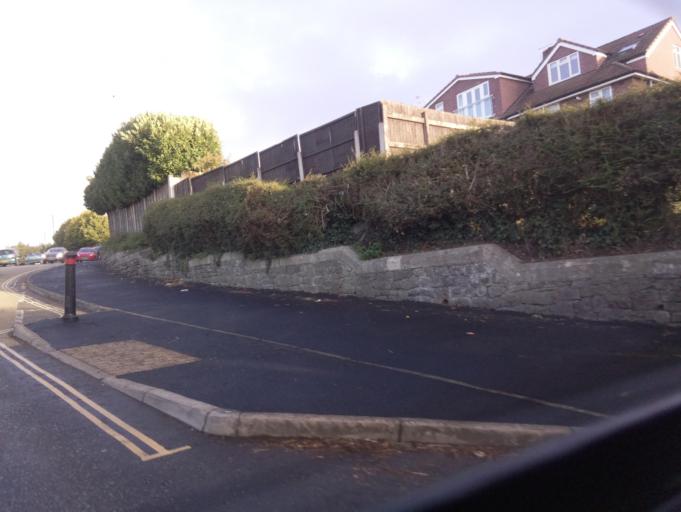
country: GB
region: England
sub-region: Bristol
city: Bristol
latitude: 51.4927
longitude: -2.6127
